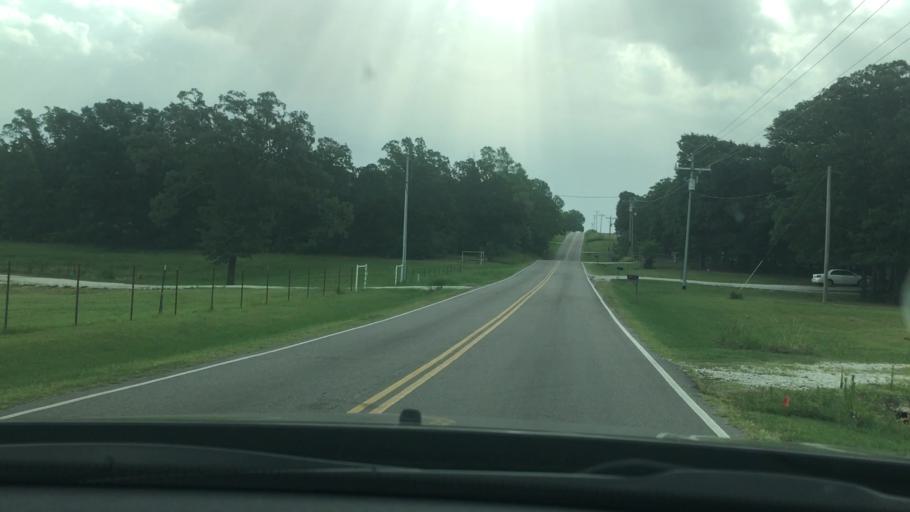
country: US
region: Oklahoma
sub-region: Pontotoc County
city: Ada
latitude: 34.8106
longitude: -96.6337
